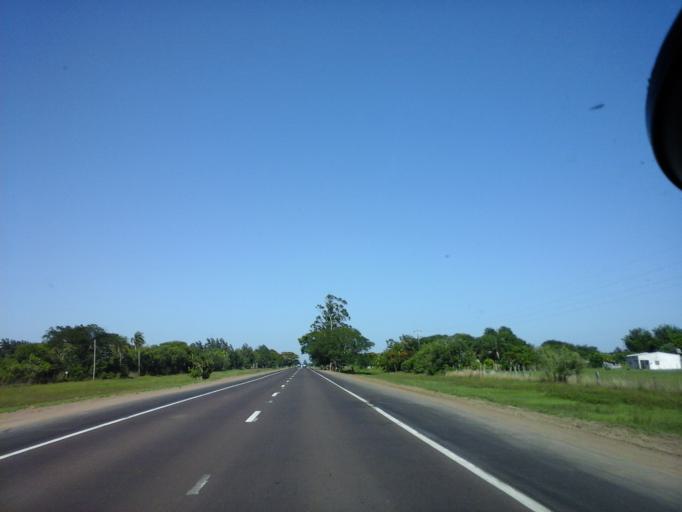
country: AR
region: Corrientes
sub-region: Departamento de Itati
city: Itati
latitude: -27.3668
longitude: -58.3385
